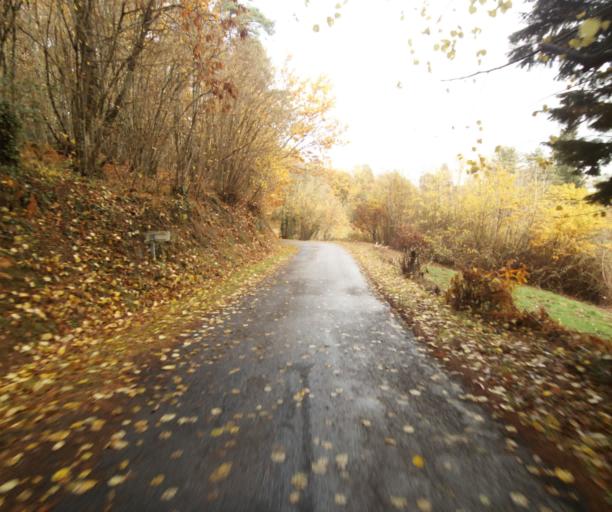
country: FR
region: Limousin
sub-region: Departement de la Correze
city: Saint-Mexant
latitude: 45.2337
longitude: 1.6356
